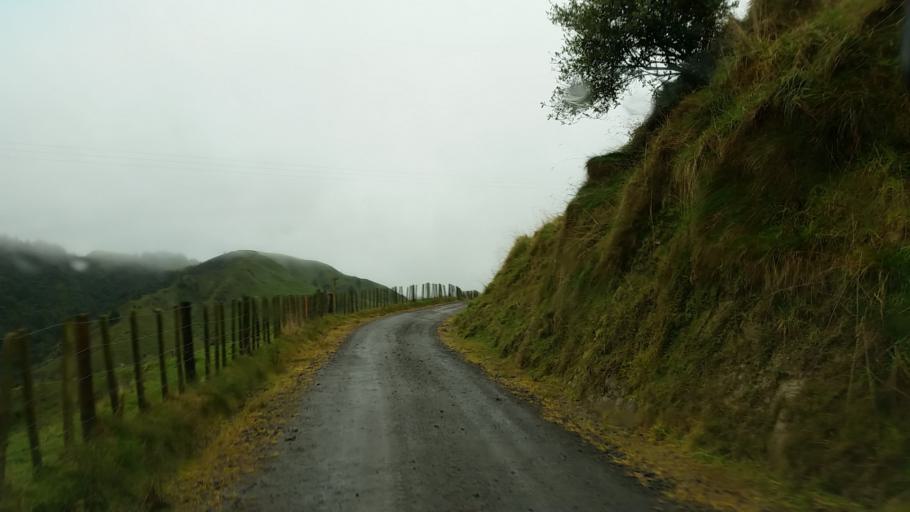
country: NZ
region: Taranaki
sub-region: South Taranaki District
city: Eltham
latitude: -39.4755
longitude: 174.4140
